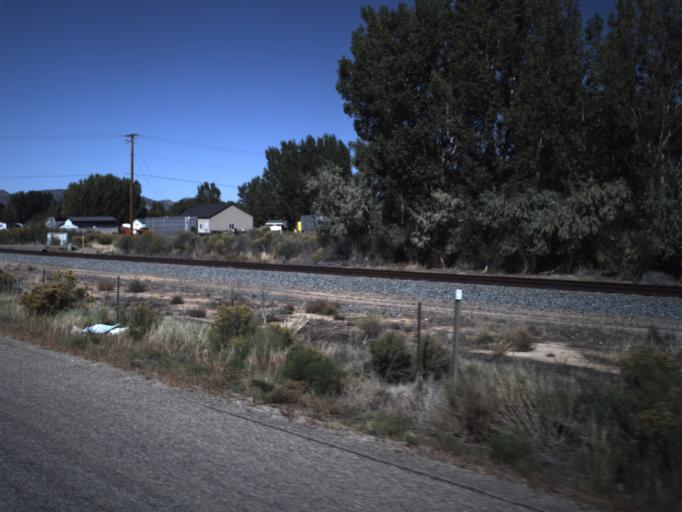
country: US
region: Utah
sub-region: Iron County
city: Cedar City
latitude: 37.6851
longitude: -113.1351
